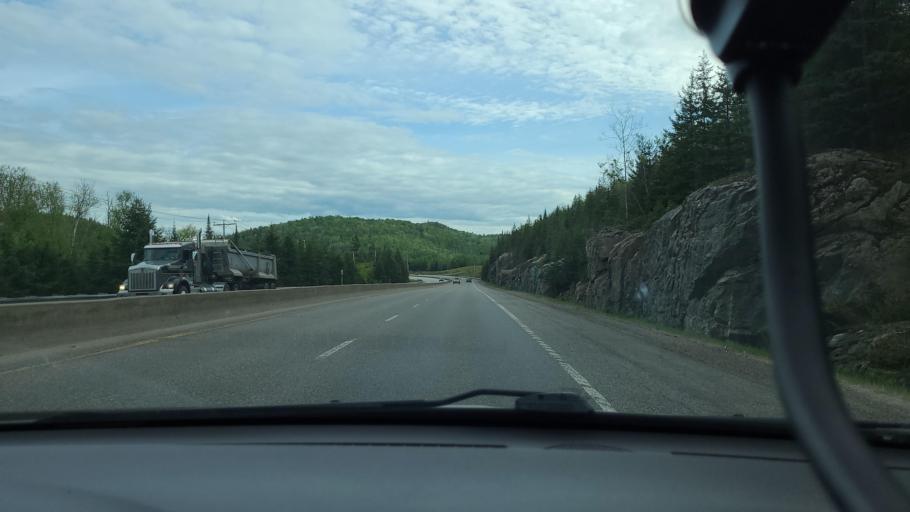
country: CA
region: Quebec
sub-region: Laurentides
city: Labelle
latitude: 46.2353
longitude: -74.7156
